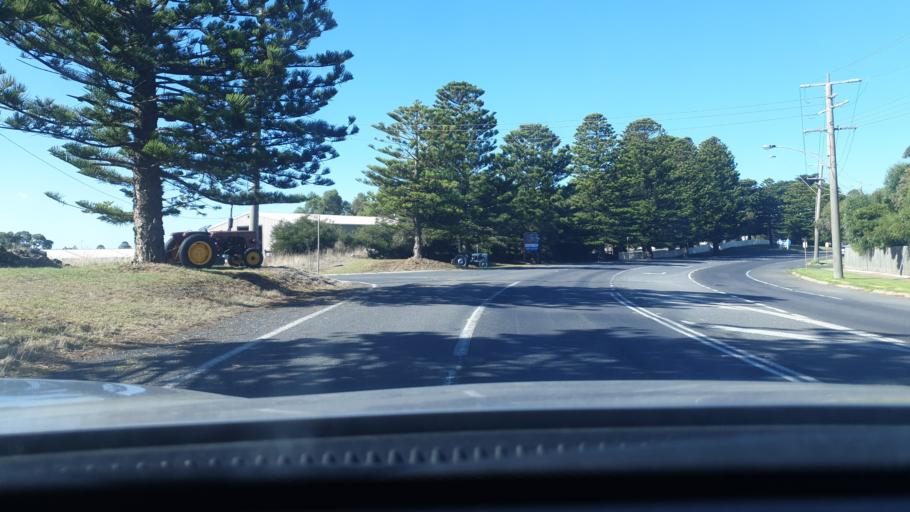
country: AU
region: Victoria
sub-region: Moyne
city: Port Fairy
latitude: -38.3849
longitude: 142.2205
